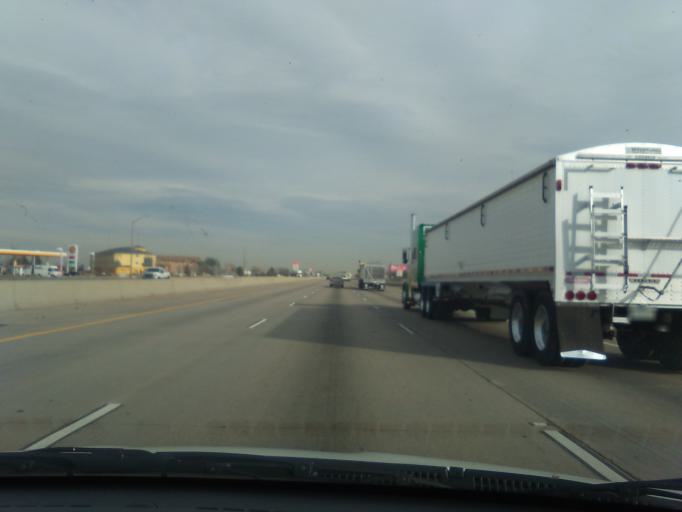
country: US
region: Colorado
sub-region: Adams County
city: Derby
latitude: 39.8585
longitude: -104.9121
